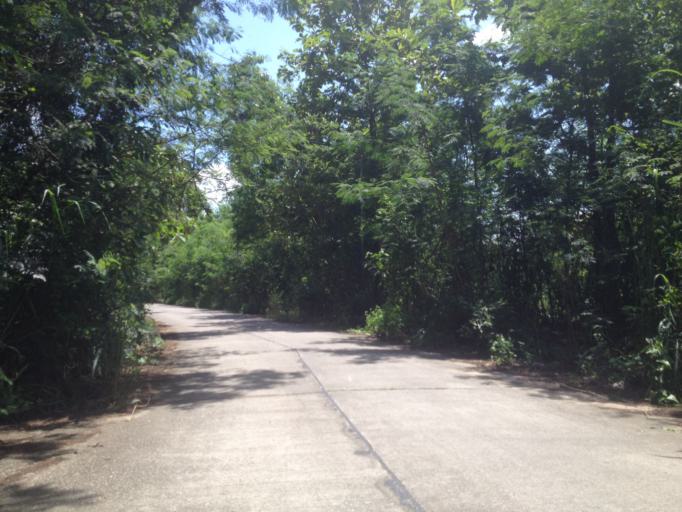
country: TH
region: Chiang Mai
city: Chiang Mai
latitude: 18.7672
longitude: 98.9375
